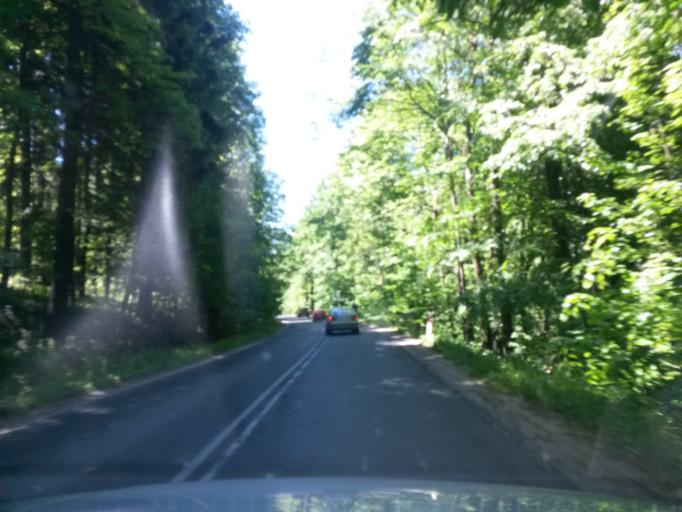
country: PL
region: Lower Silesian Voivodeship
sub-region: Powiat jeleniogorski
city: Kowary
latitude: 50.7836
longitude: 15.8647
